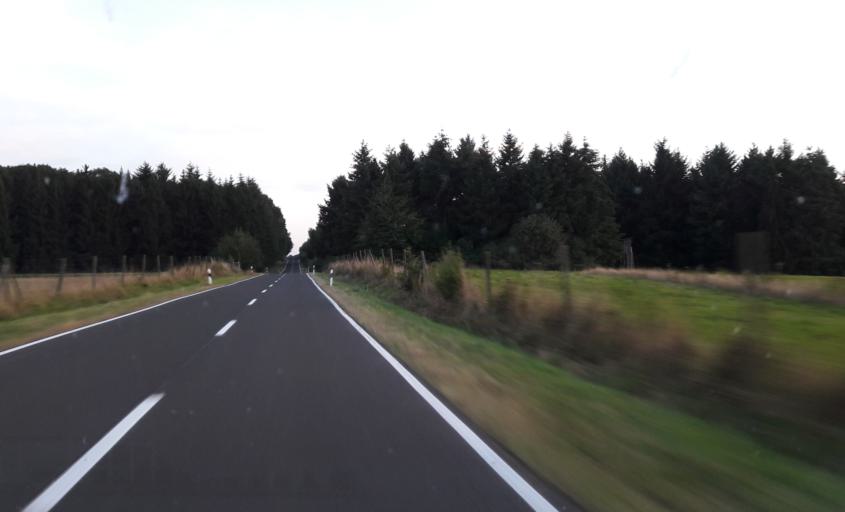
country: DE
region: Rheinland-Pfalz
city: Krov
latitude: 50.0039
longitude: 7.0860
